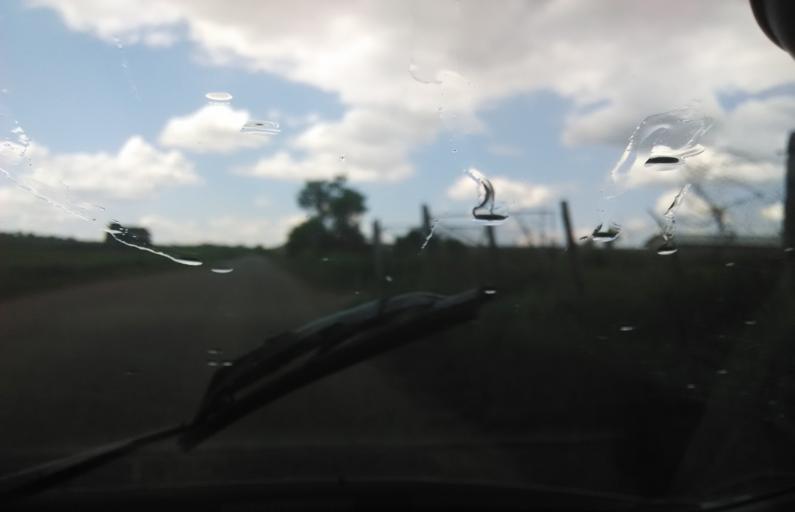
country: SK
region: Nitriansky
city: Levice
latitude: 48.1973
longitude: 18.6558
